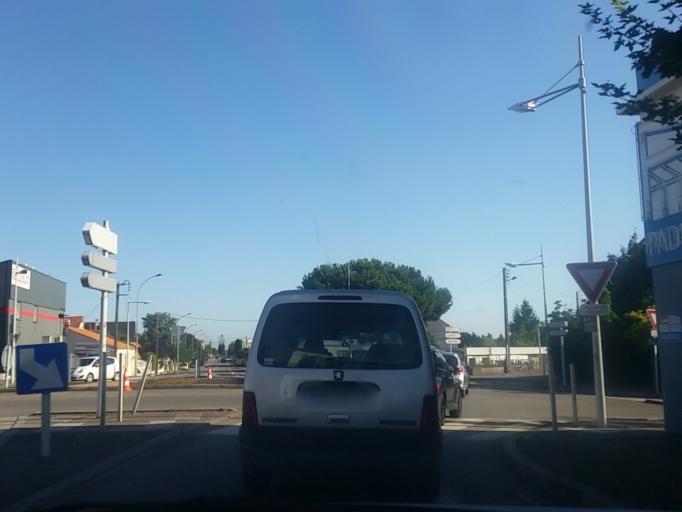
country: FR
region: Pays de la Loire
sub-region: Departement de la Loire-Atlantique
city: Reze
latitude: 47.1681
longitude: -1.5429
